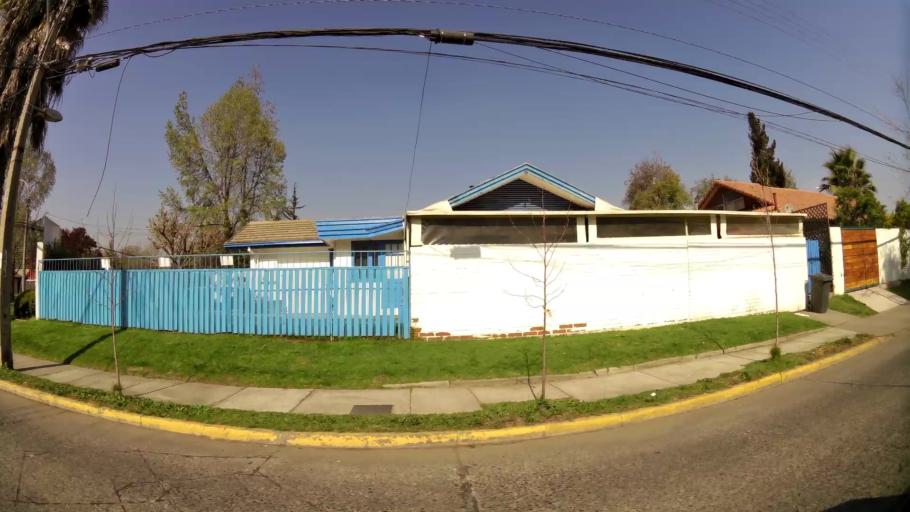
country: CL
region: Santiago Metropolitan
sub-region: Provincia de Santiago
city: Villa Presidente Frei, Nunoa, Santiago, Chile
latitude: -33.3794
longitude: -70.5558
